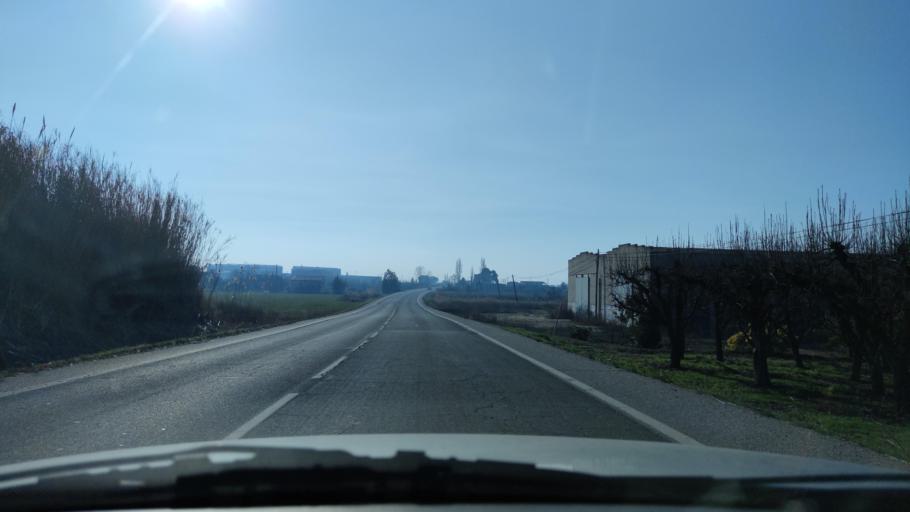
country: ES
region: Catalonia
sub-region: Provincia de Lleida
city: Torrefarrera
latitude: 41.6518
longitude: 0.6348
